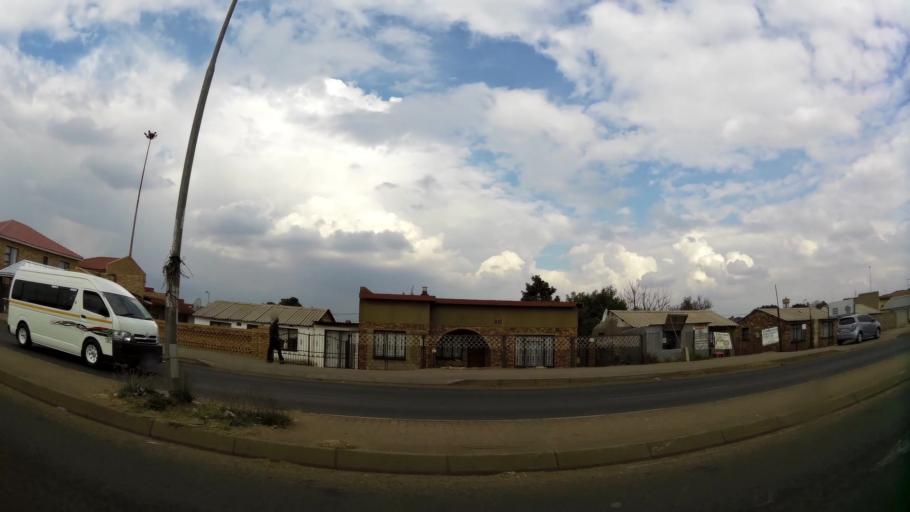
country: ZA
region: Gauteng
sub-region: City of Johannesburg Metropolitan Municipality
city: Soweto
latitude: -26.2367
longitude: 27.8613
